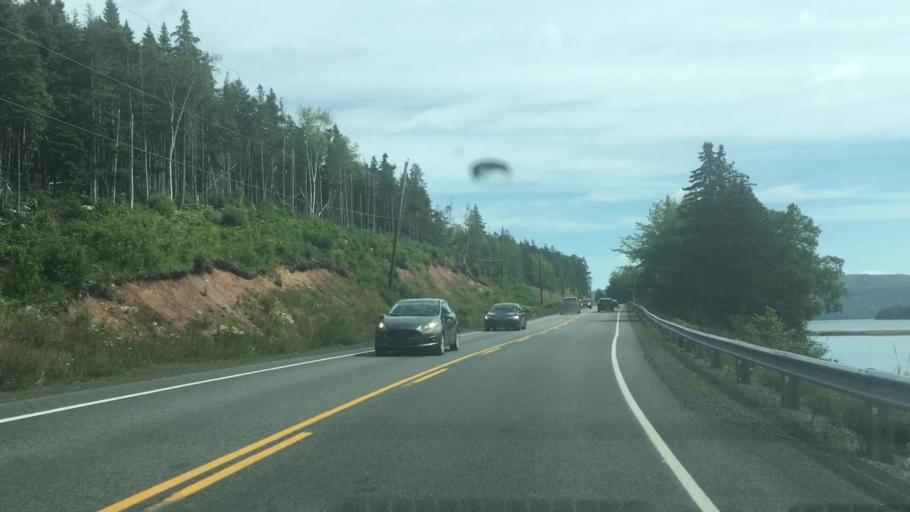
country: CA
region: Nova Scotia
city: Sydney Mines
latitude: 46.2663
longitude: -60.6187
